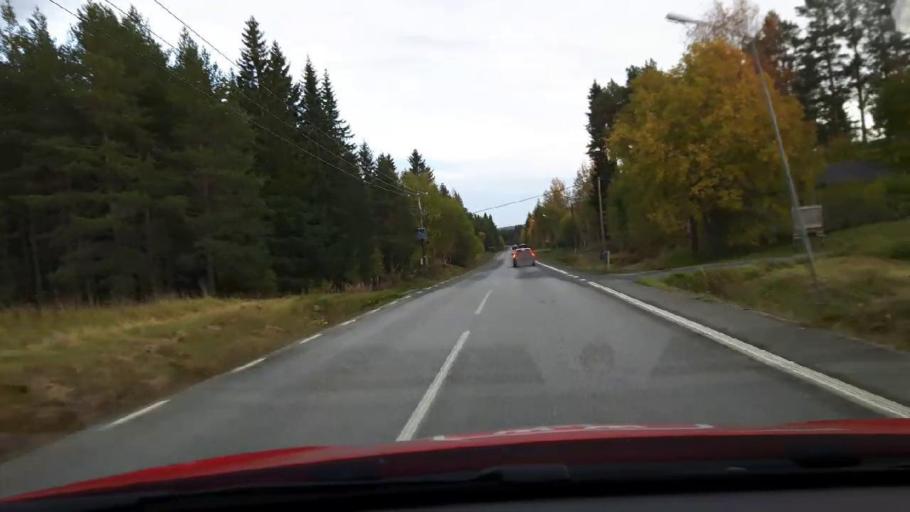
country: SE
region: Jaemtland
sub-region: Krokoms Kommun
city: Krokom
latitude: 63.3356
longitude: 14.6004
